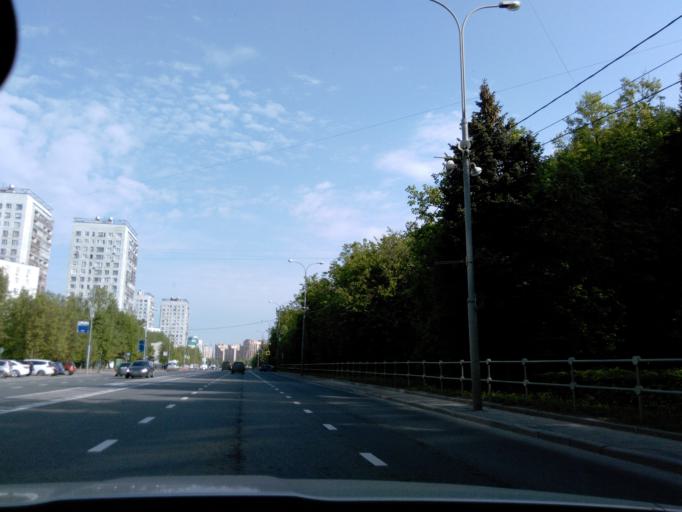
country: RU
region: Moscow
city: Zelenograd
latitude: 55.9963
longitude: 37.2123
